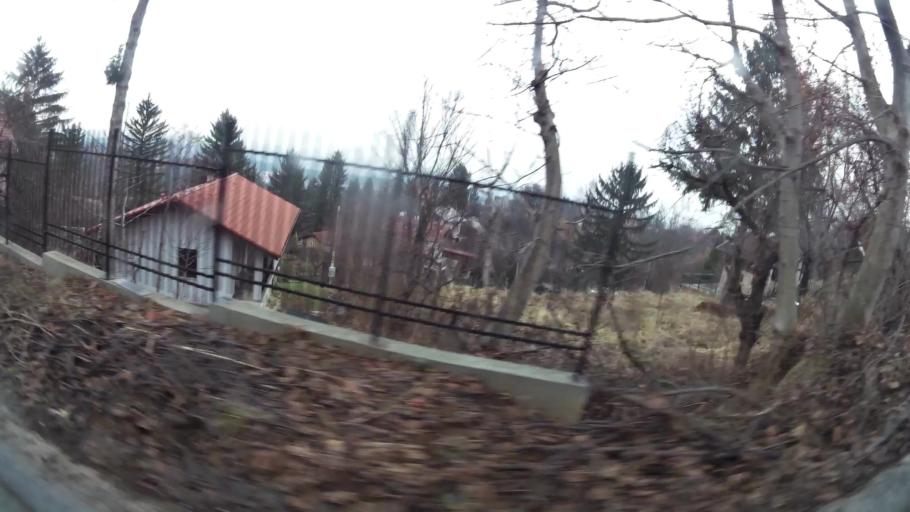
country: BG
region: Sofia-Capital
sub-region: Stolichna Obshtina
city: Sofia
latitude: 42.6001
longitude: 23.3878
